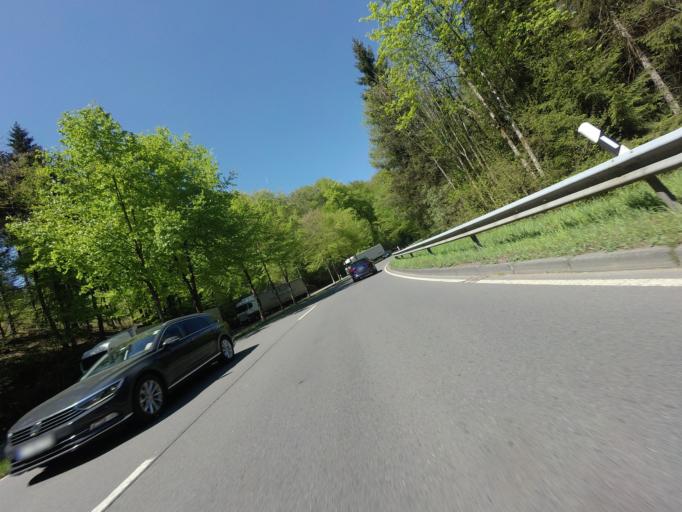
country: DE
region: North Rhine-Westphalia
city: Kreuztal
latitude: 51.0011
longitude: 7.9397
